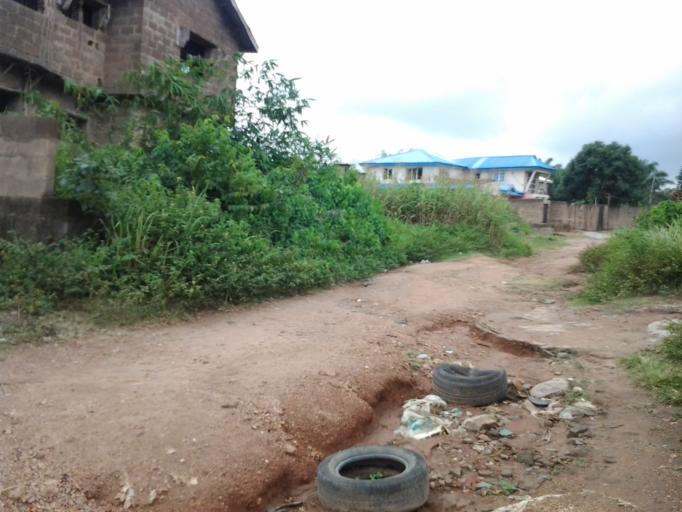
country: NG
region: Oyo
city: Ibadan
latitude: 7.4339
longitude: 3.9591
